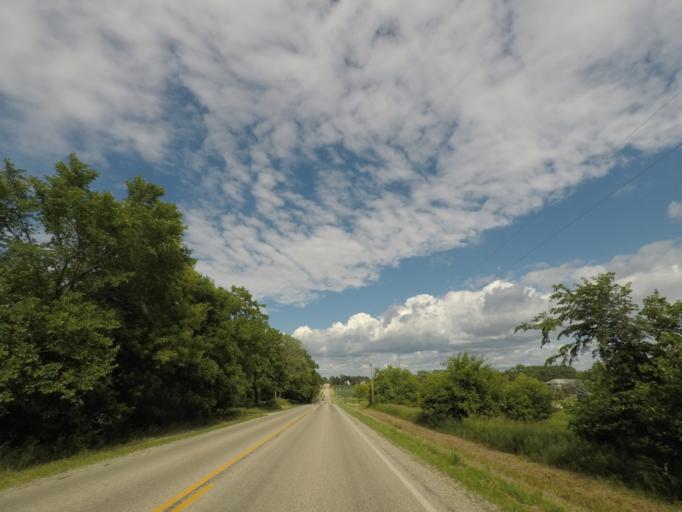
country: US
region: Wisconsin
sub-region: Rock County
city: Janesville
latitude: 42.7012
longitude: -89.1055
